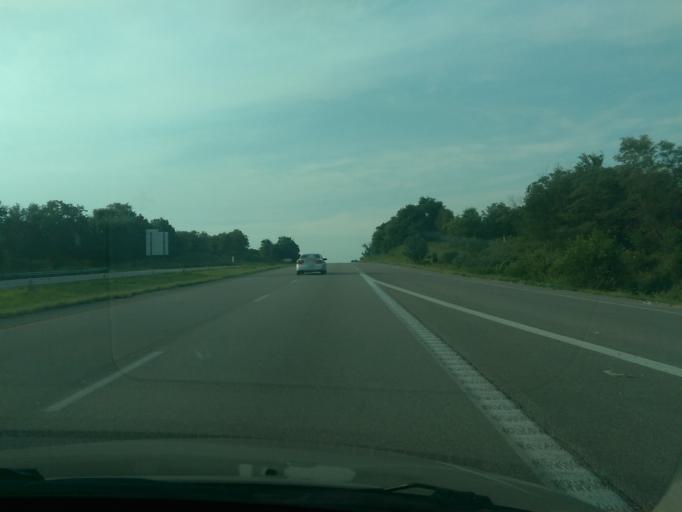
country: US
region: Missouri
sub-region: Platte County
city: Platte City
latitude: 39.3872
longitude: -94.7894
